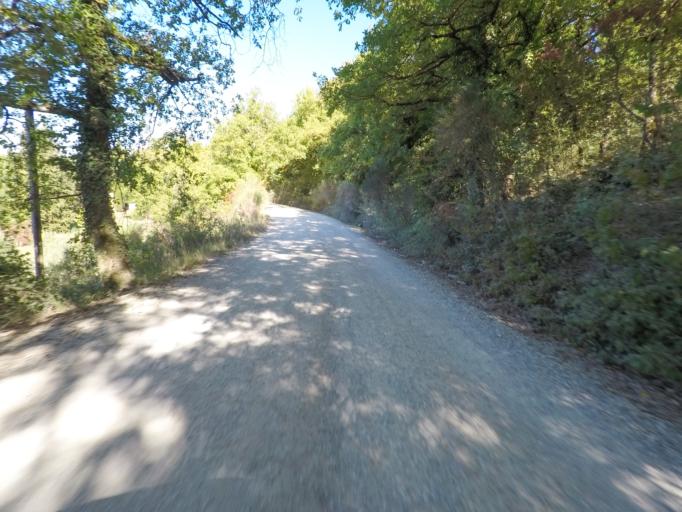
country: IT
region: Tuscany
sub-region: Provincia di Siena
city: Castellina in Chianti
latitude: 43.4303
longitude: 11.3336
